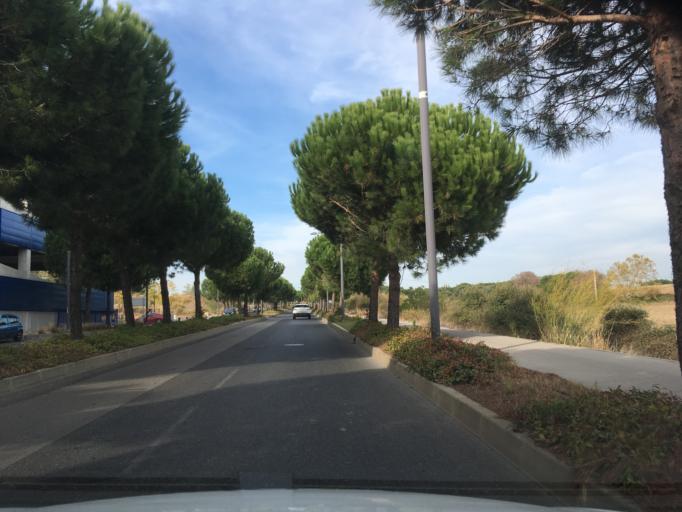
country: FR
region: Languedoc-Roussillon
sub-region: Departement de l'Herault
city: Castelnau-le-Lez
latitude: 43.6045
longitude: 3.9262
